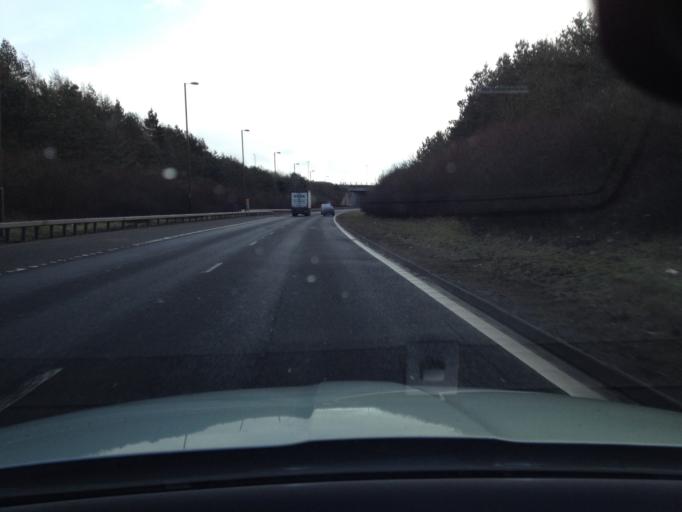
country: GB
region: Scotland
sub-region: Edinburgh
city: Newbridge
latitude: 55.9285
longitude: -3.4033
